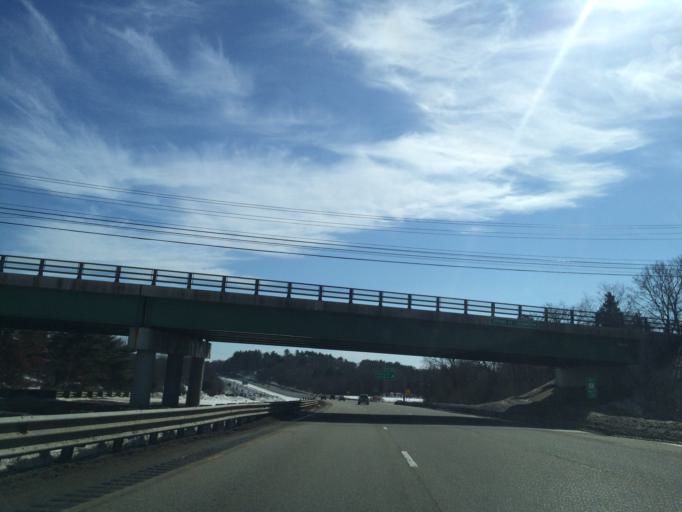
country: US
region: Massachusetts
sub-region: Middlesex County
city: Lexington
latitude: 42.4241
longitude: -71.2517
